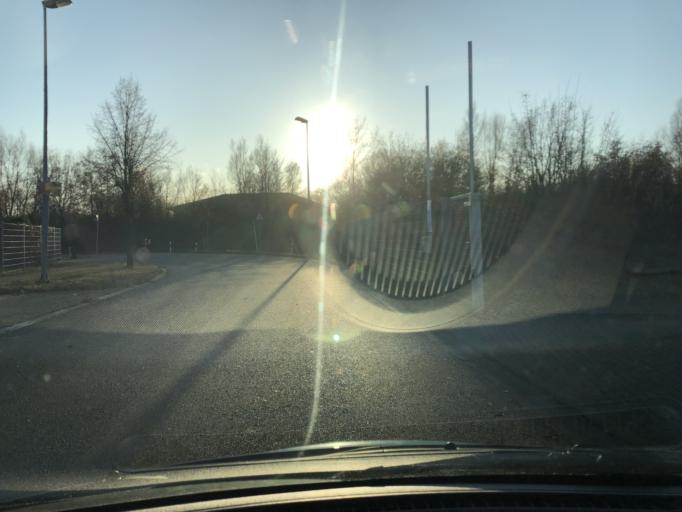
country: DE
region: Lower Saxony
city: Winsen
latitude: 53.3411
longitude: 10.2281
